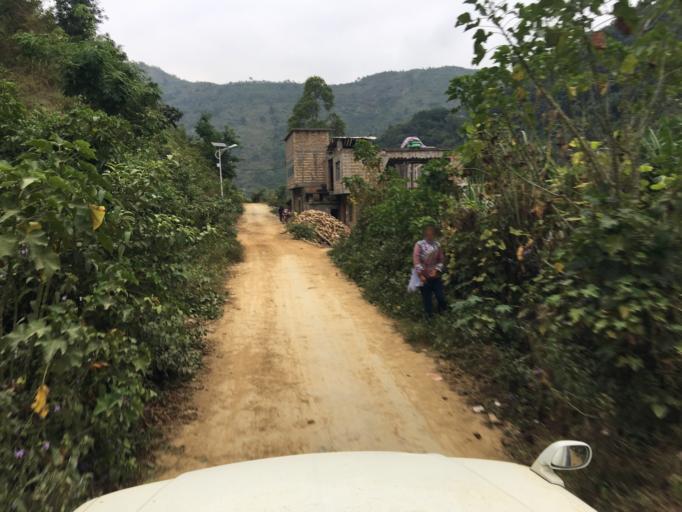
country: CN
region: Guangxi Zhuangzu Zizhiqu
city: Leli
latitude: 24.7654
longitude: 106.0892
